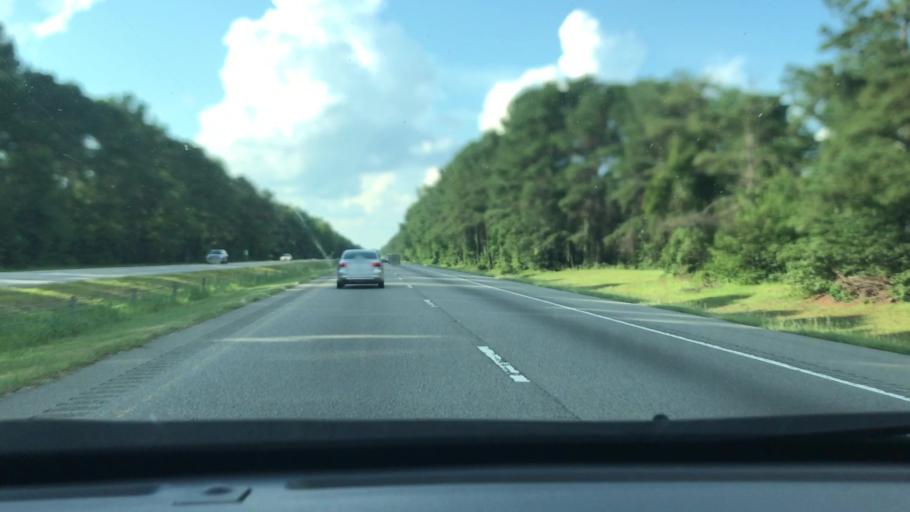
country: US
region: North Carolina
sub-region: Robeson County
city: Saint Pauls
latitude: 34.7327
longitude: -78.9972
